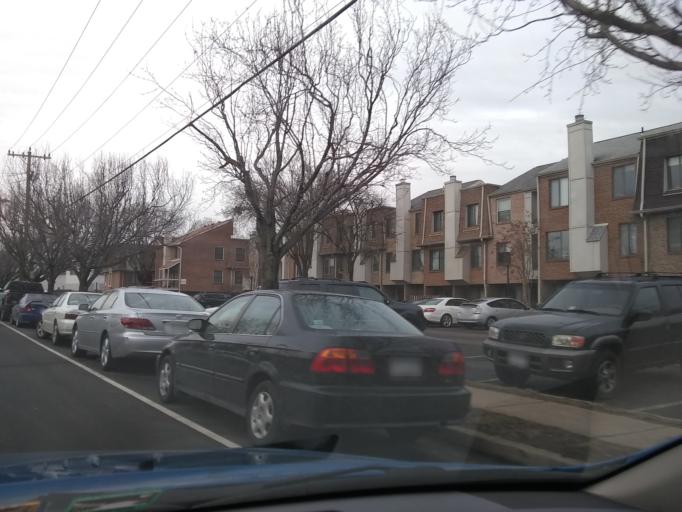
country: US
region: Virginia
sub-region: Fairfax County
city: Huntington
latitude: 38.8305
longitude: -77.0834
